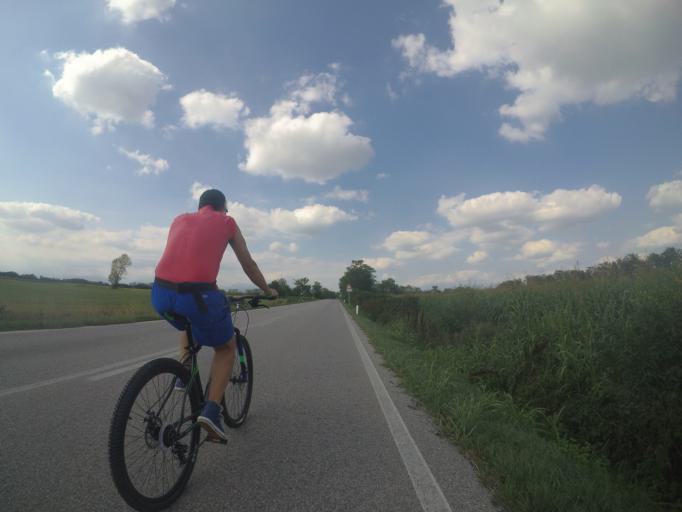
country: IT
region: Friuli Venezia Giulia
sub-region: Provincia di Udine
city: San Vito di Fagagna
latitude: 46.0799
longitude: 13.0860
